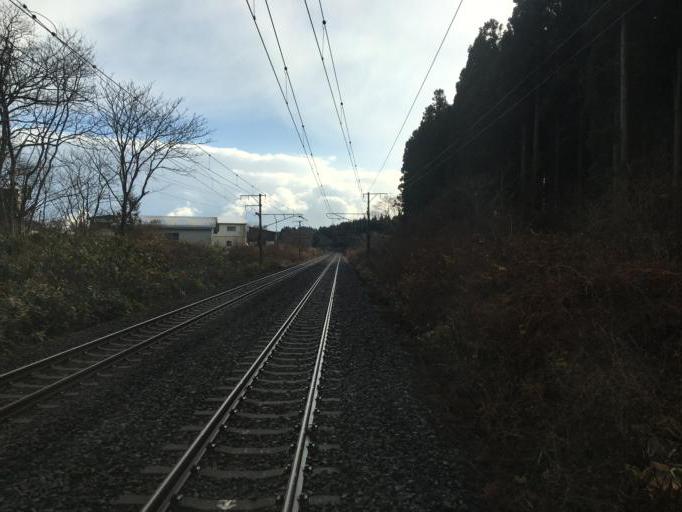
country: JP
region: Aomori
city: Aomori Shi
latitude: 40.9163
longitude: 141.0343
